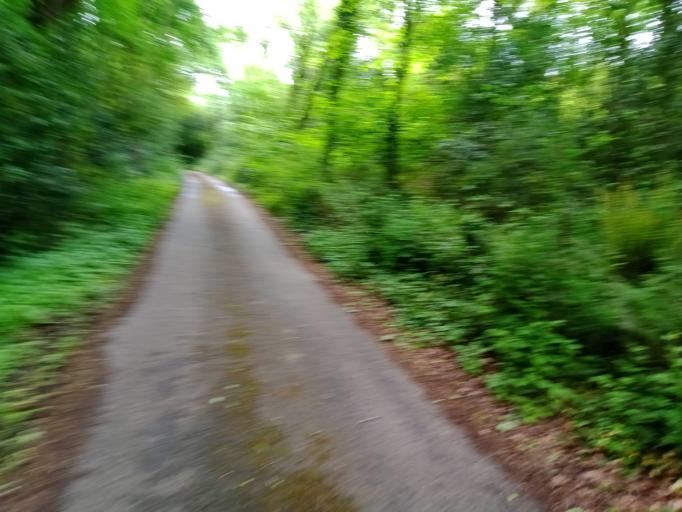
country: IE
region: Leinster
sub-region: Kilkenny
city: Thomastown
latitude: 52.5073
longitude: -7.1304
